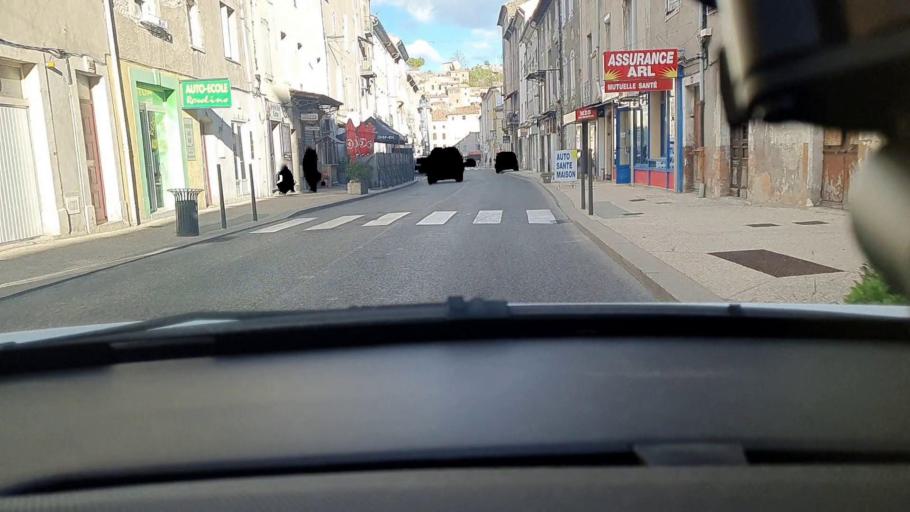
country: FR
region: Languedoc-Roussillon
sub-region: Departement du Gard
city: Saint-Ambroix
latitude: 44.2597
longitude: 4.2003
